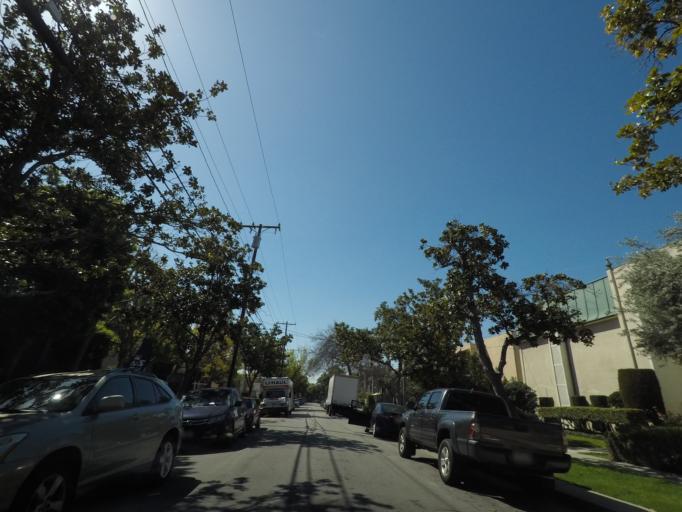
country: US
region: California
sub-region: Los Angeles County
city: Pasadena
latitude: 34.1315
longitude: -118.1443
